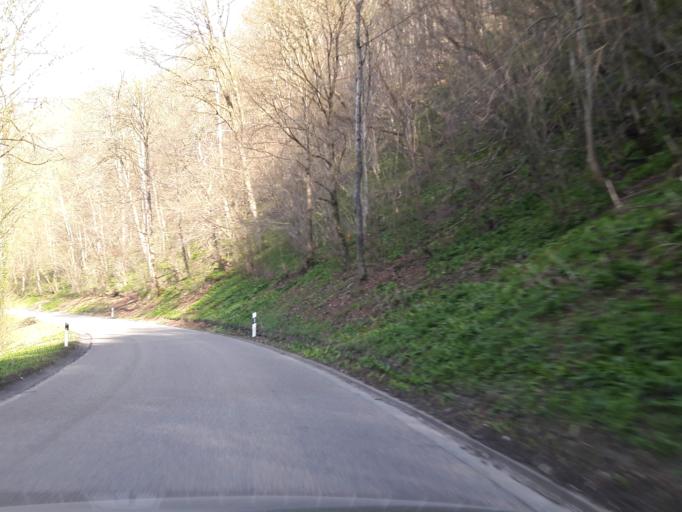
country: DE
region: Baden-Wuerttemberg
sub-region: Regierungsbezirk Stuttgart
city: Ohringen
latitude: 49.2284
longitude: 9.4711
